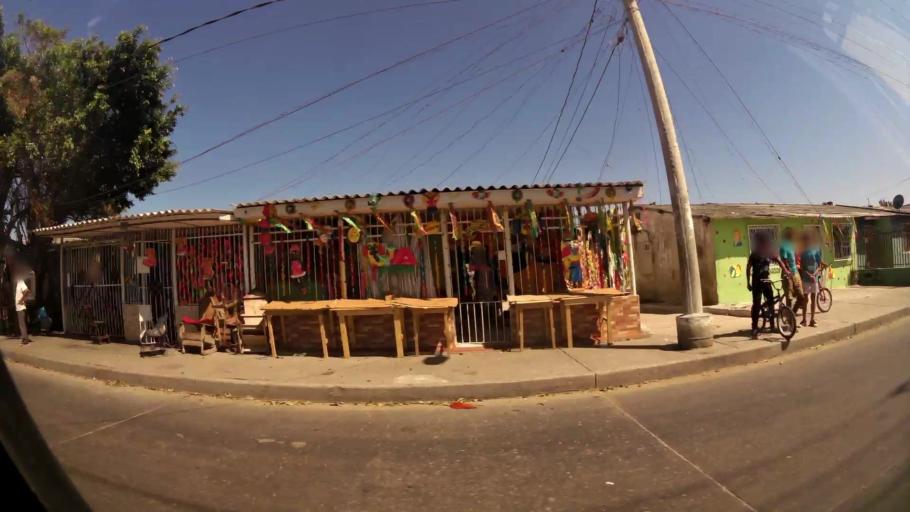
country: CO
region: Atlantico
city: Barranquilla
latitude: 10.9699
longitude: -74.7744
